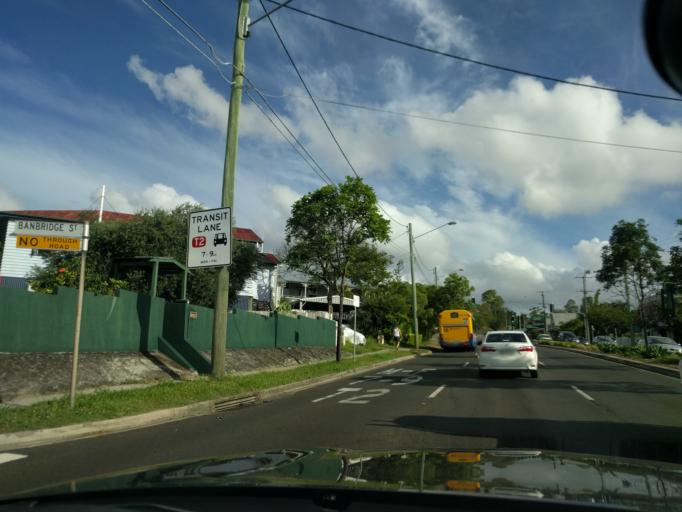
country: AU
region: Queensland
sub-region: Brisbane
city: Wilston
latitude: -27.4473
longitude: 153.0099
